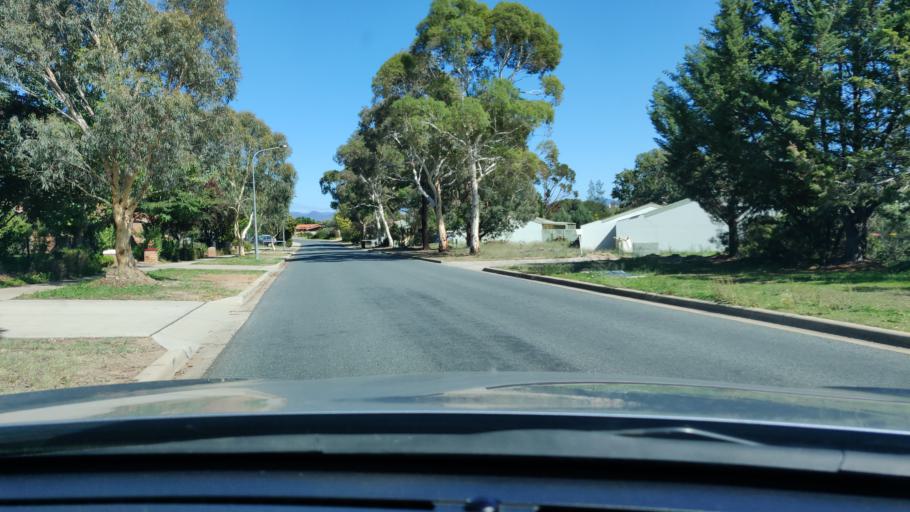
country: AU
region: Australian Capital Territory
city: Macarthur
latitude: -35.4384
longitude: 149.0979
